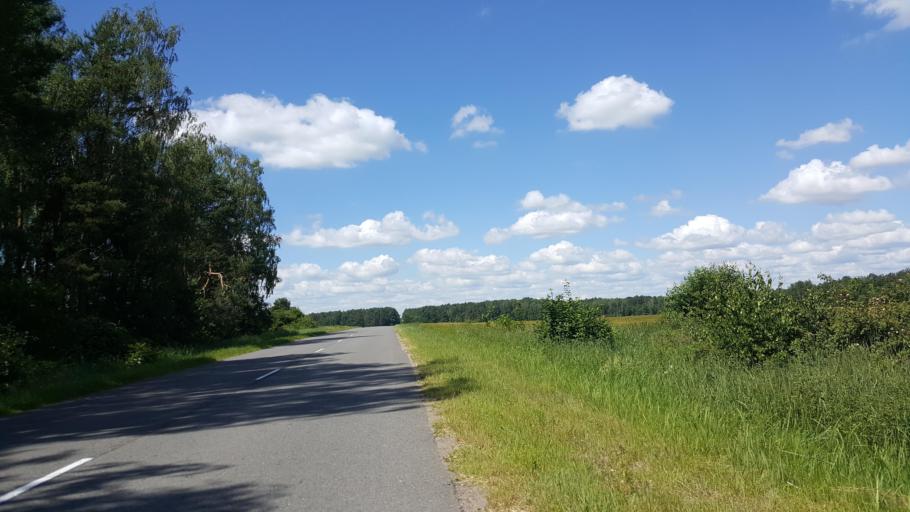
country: BY
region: Brest
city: Kamyanyets
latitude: 52.3786
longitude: 23.6394
